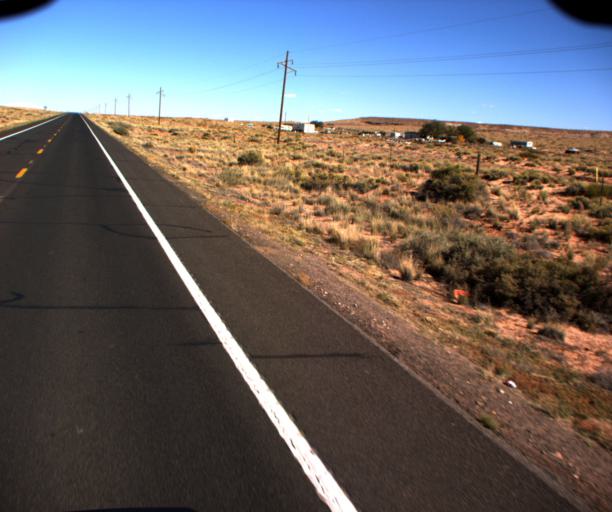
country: US
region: Arizona
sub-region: Coconino County
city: Tuba City
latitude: 36.1304
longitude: -111.1893
